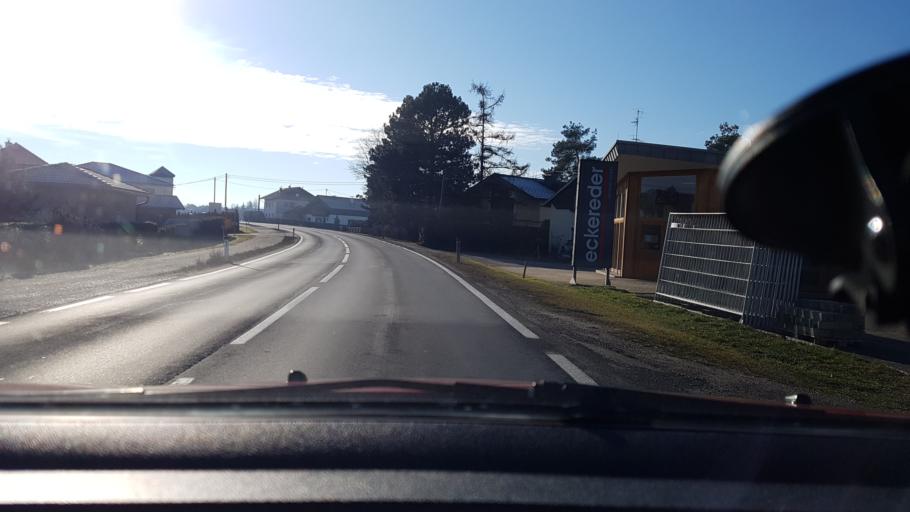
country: AT
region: Upper Austria
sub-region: Politischer Bezirk Braunau am Inn
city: Braunau am Inn
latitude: 48.1841
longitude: 13.0557
